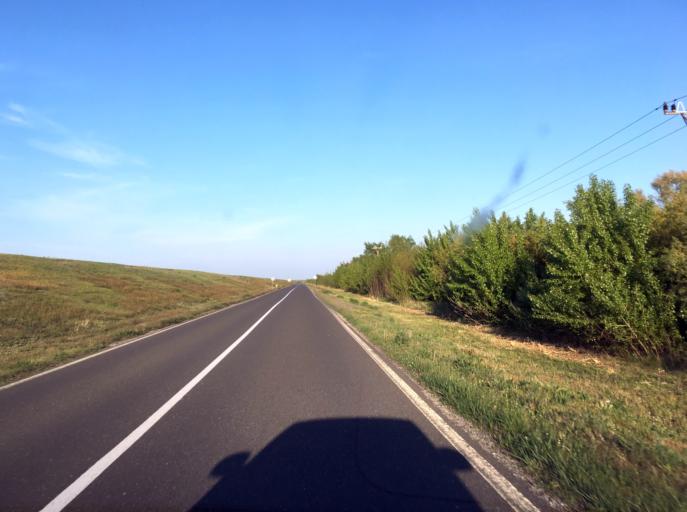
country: SK
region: Trnavsky
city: Samorin
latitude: 47.9974
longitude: 17.3039
